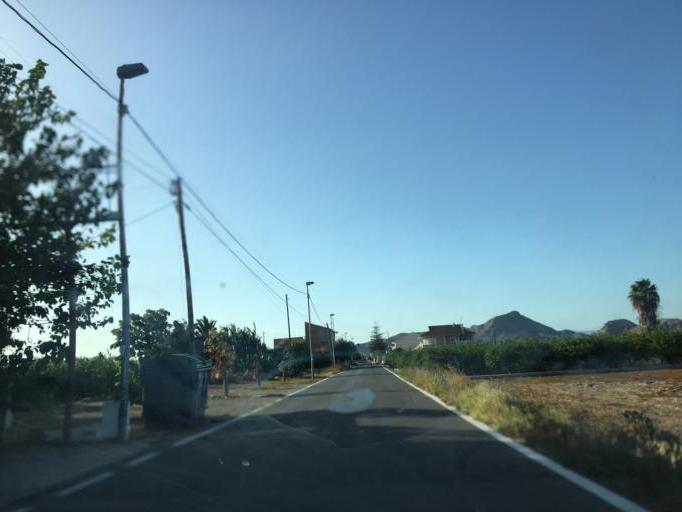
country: ES
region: Murcia
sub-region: Murcia
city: Santomera
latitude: 38.0260
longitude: -1.0565
